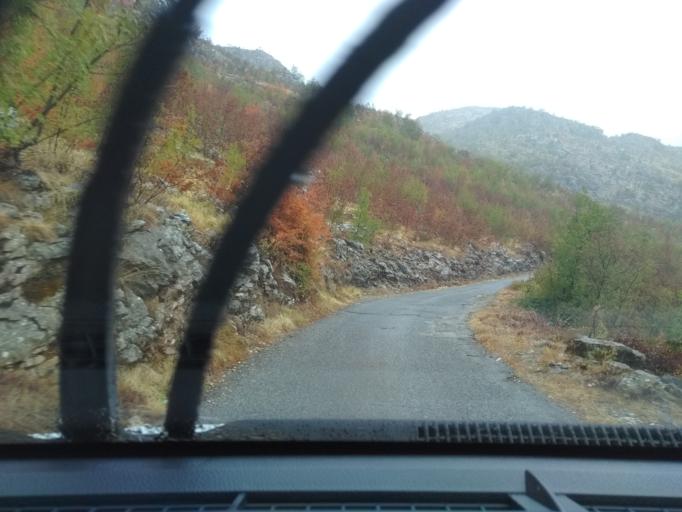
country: ME
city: Stari Bar
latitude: 42.1701
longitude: 19.1922
